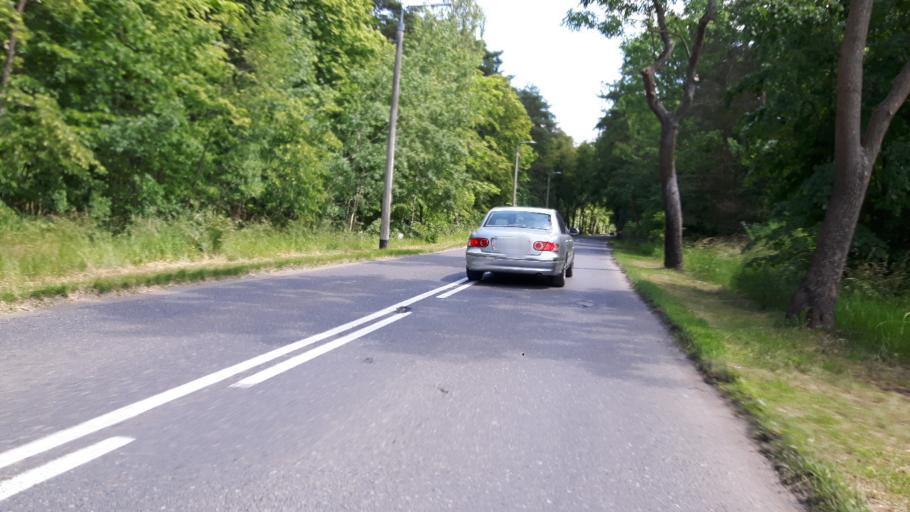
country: PL
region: Pomeranian Voivodeship
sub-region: Powiat gdanski
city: Cedry Wielkie
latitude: 54.3408
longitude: 18.8781
